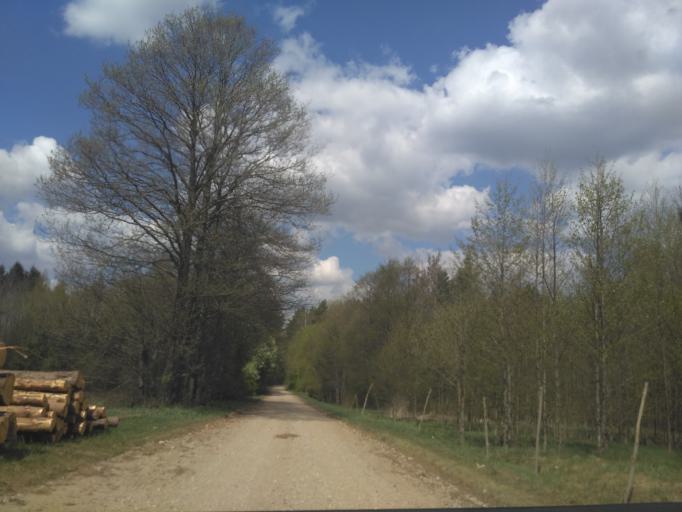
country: BY
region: Minsk
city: Il'ya
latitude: 54.2838
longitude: 27.2978
